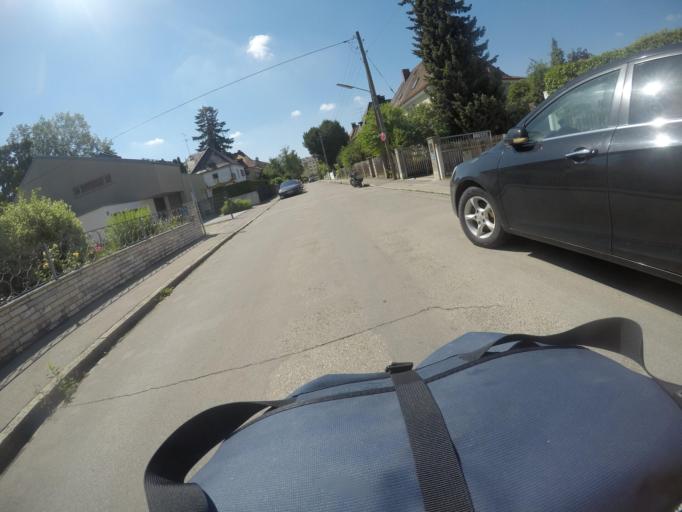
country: DE
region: Bavaria
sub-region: Upper Bavaria
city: Karlsfeld
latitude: 48.1834
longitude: 11.5131
